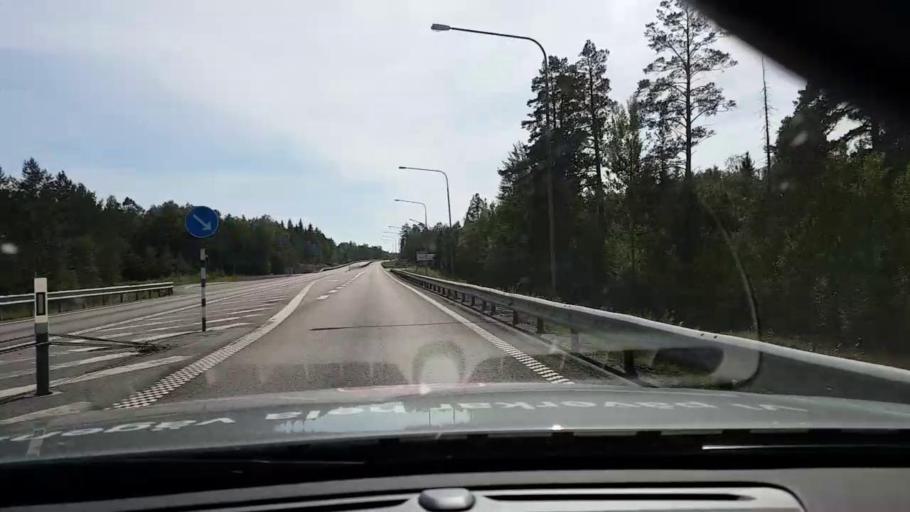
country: SE
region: Vaesternorrland
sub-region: OErnskoeldsviks Kommun
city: Husum
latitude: 63.3763
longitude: 19.1903
